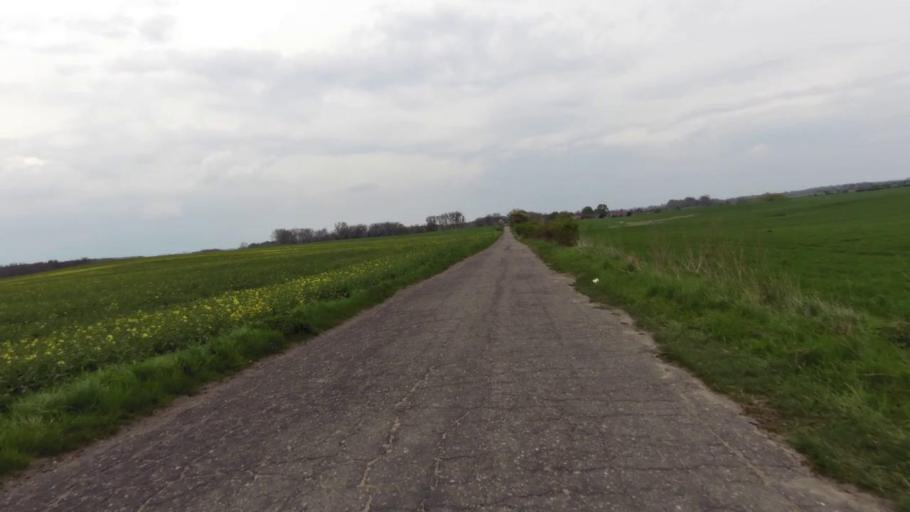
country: PL
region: West Pomeranian Voivodeship
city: Trzcinsko Zdroj
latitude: 52.9473
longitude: 14.7079
